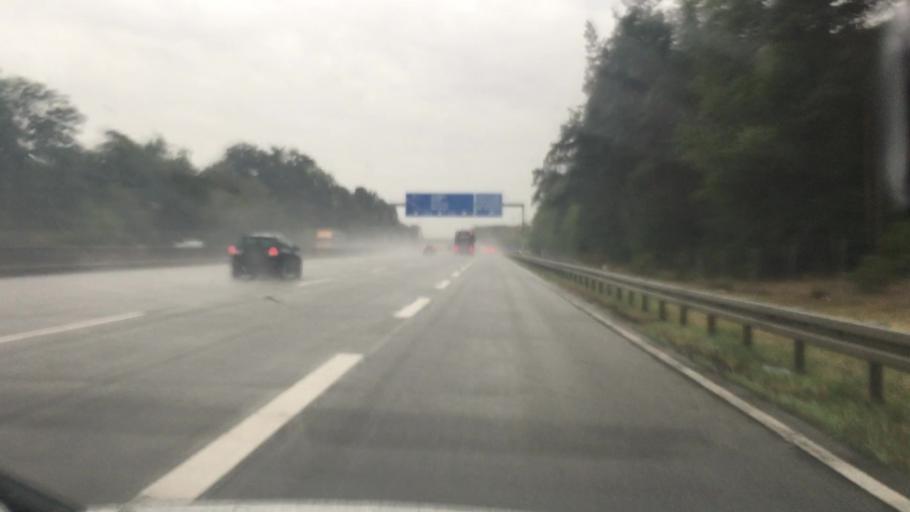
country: DE
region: Hesse
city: Viernheim
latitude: 49.5639
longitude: 8.5585
